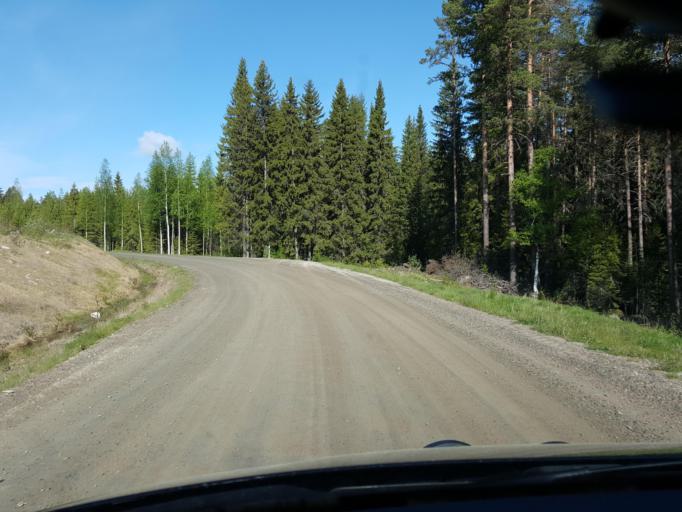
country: SE
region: Vaesternorrland
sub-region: Ange Kommun
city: Ange
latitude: 62.1798
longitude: 15.6267
